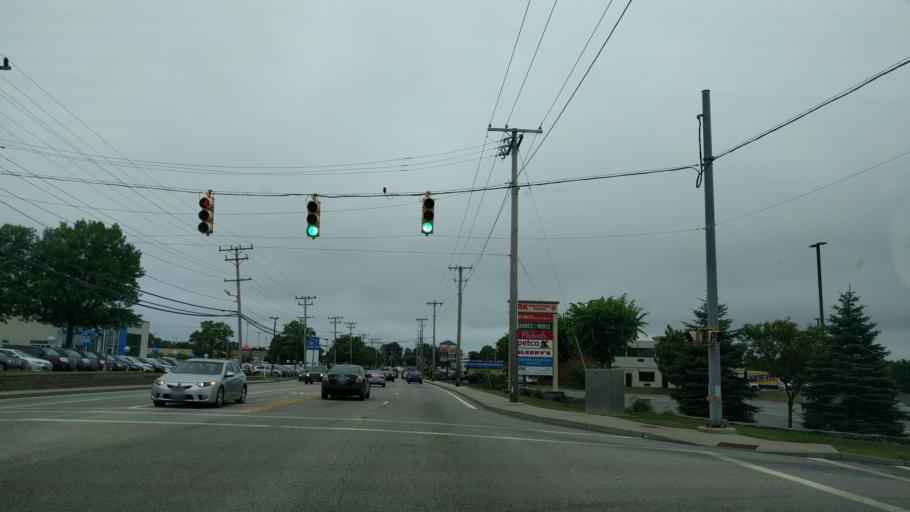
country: US
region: Rhode Island
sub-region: Newport County
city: Middletown
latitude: 41.5347
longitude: -71.2926
